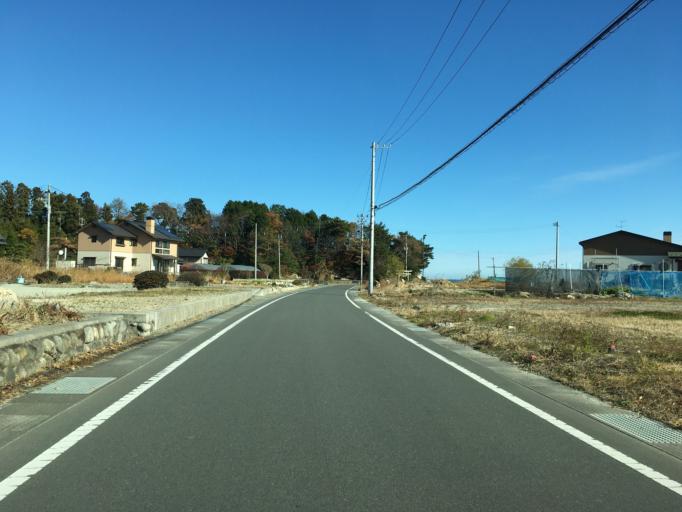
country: JP
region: Miyagi
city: Marumori
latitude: 37.8061
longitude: 140.9707
